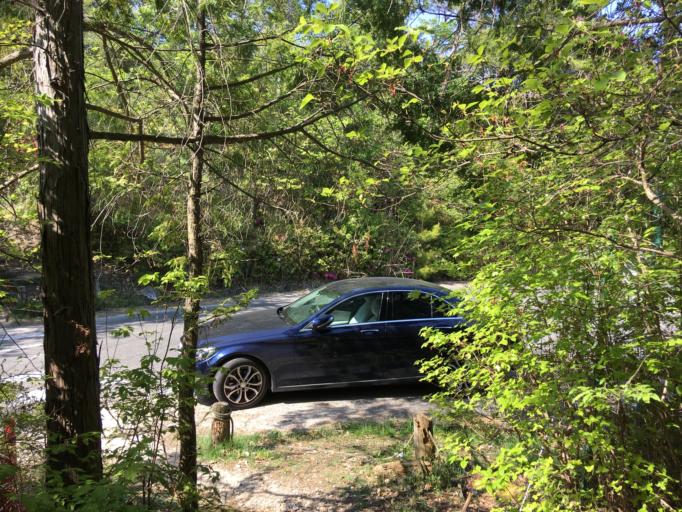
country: JP
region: Nara
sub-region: Ikoma-shi
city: Ikoma
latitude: 34.6962
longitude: 135.7169
